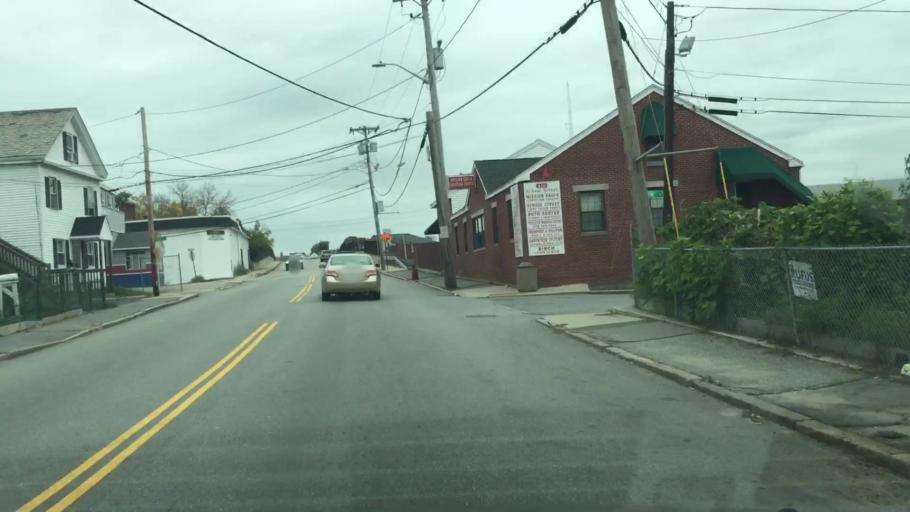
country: US
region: Massachusetts
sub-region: Middlesex County
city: Lowell
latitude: 42.6392
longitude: -71.3248
